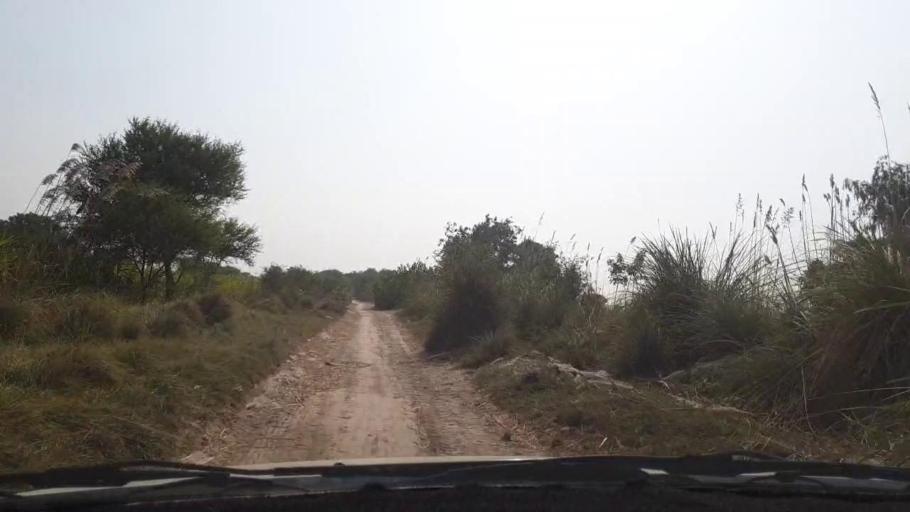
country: PK
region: Sindh
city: Tando Muhammad Khan
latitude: 25.0818
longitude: 68.3604
